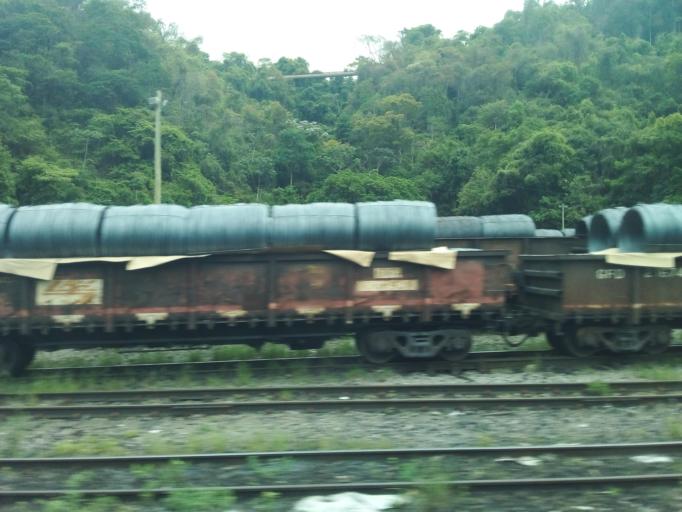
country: BR
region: Minas Gerais
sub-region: Joao Monlevade
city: Joao Monlevade
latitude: -19.8427
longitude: -43.1271
